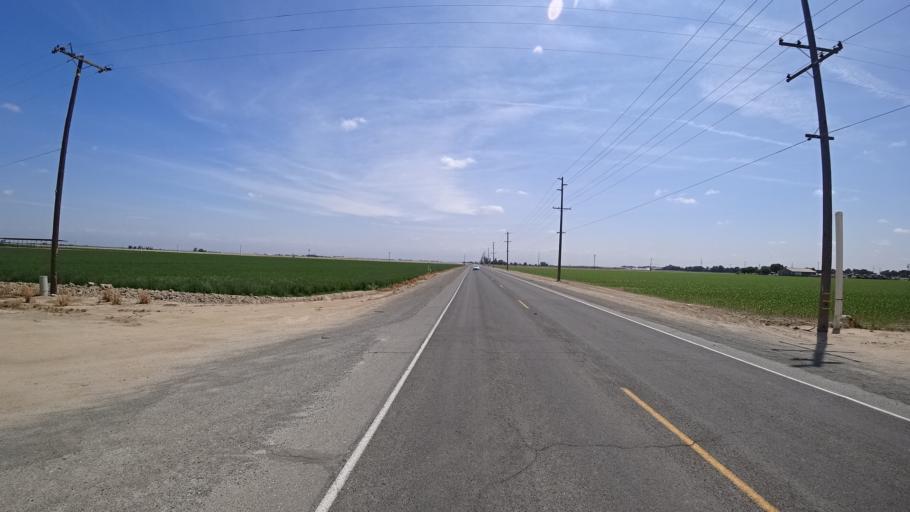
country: US
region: California
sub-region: Tulare County
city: Goshen
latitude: 36.2979
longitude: -119.4788
